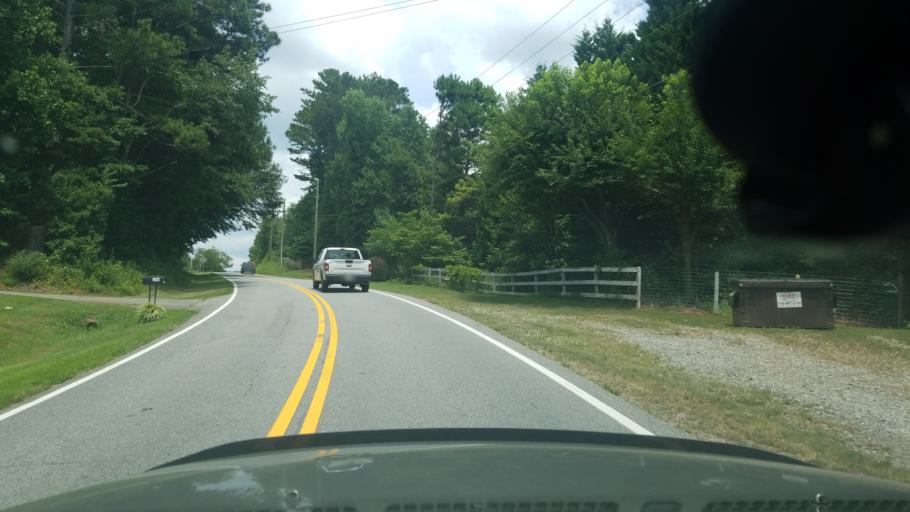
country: US
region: Georgia
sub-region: Forsyth County
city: Cumming
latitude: 34.2125
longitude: -84.2036
